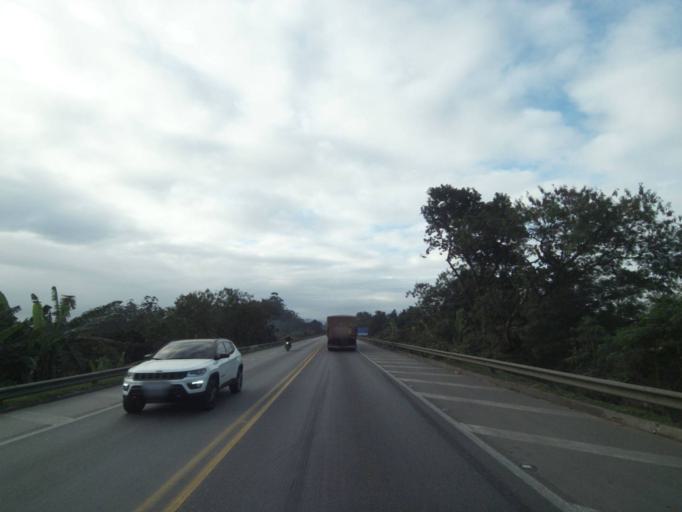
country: BR
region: Parana
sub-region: Paranagua
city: Paranagua
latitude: -25.5503
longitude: -48.5613
